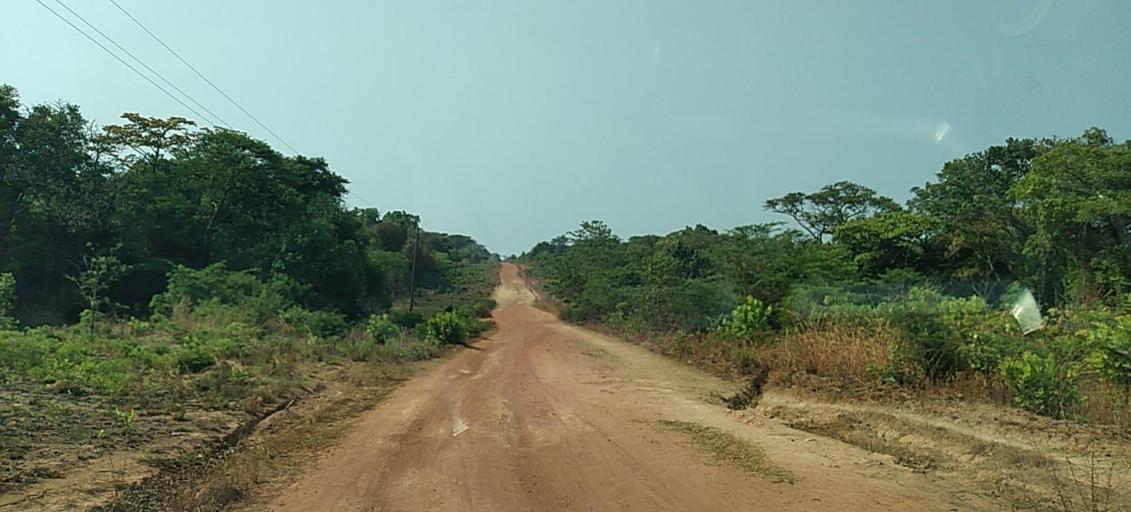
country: ZM
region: Copperbelt
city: Chingola
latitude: -12.9079
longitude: 27.3716
